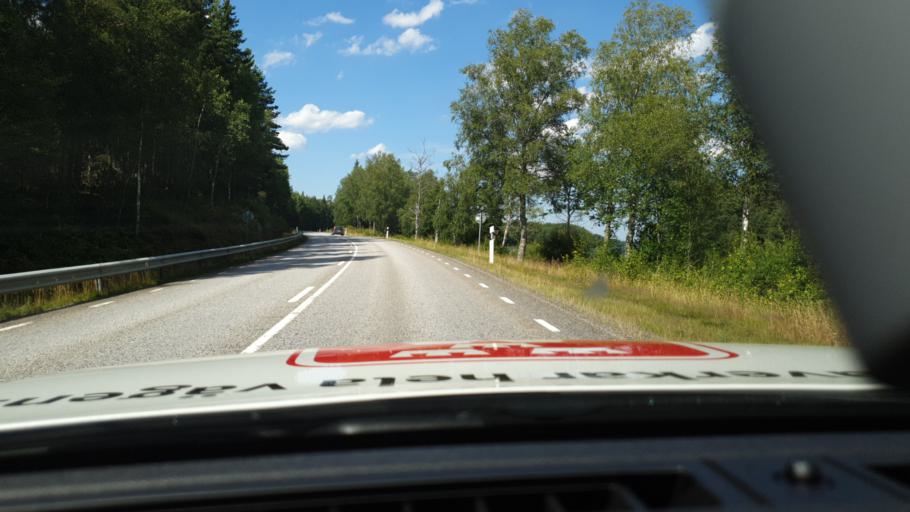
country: SE
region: Joenkoeping
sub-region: Vaggeryds Kommun
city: Vaggeryd
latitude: 57.5402
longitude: 14.2671
